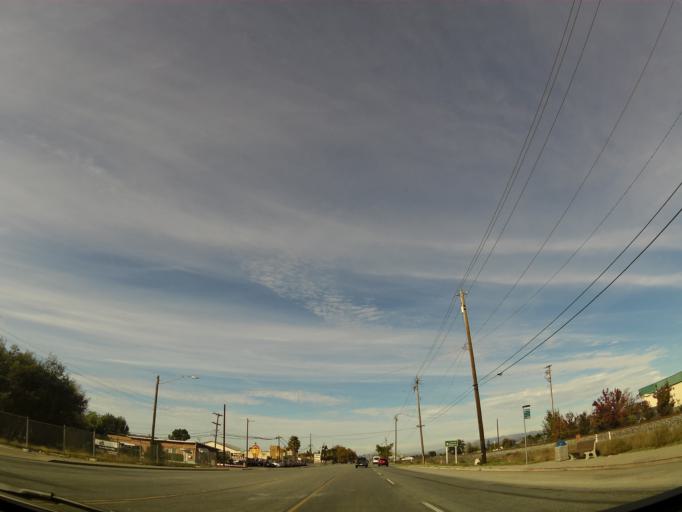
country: US
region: California
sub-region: Santa Clara County
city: Gilroy
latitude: 37.0255
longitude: -121.5779
